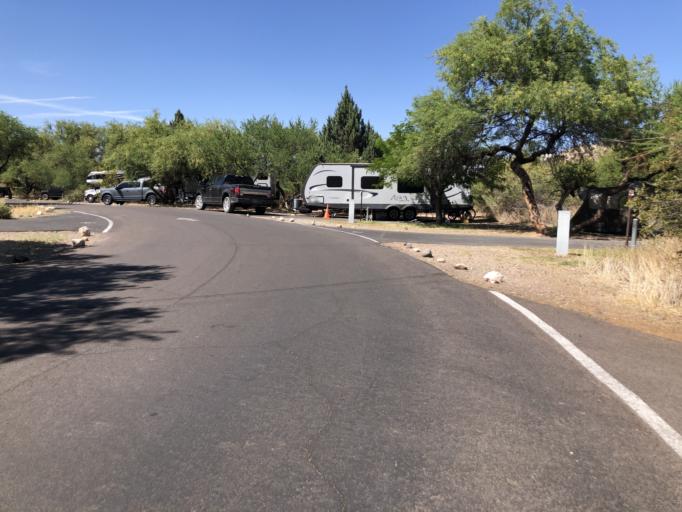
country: US
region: Arizona
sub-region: Yavapai County
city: Cottonwood
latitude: 34.7538
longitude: -112.0165
